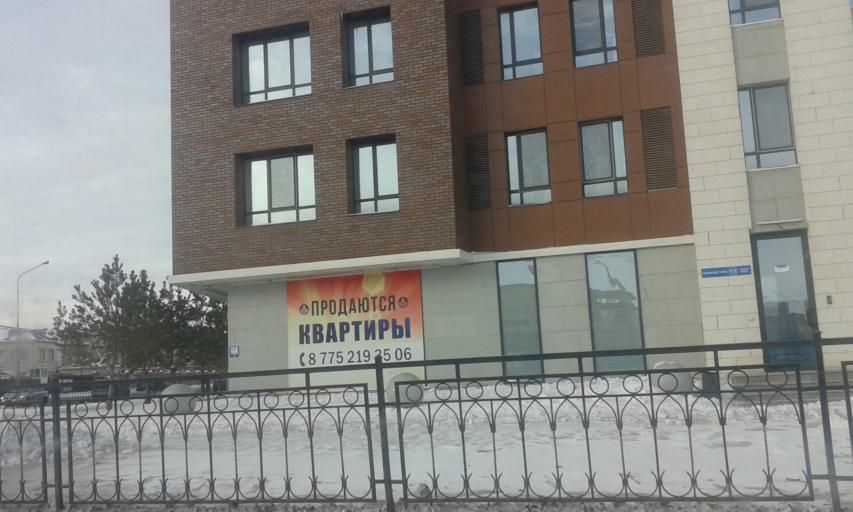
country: KZ
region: Astana Qalasy
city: Astana
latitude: 51.1430
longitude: 71.4543
